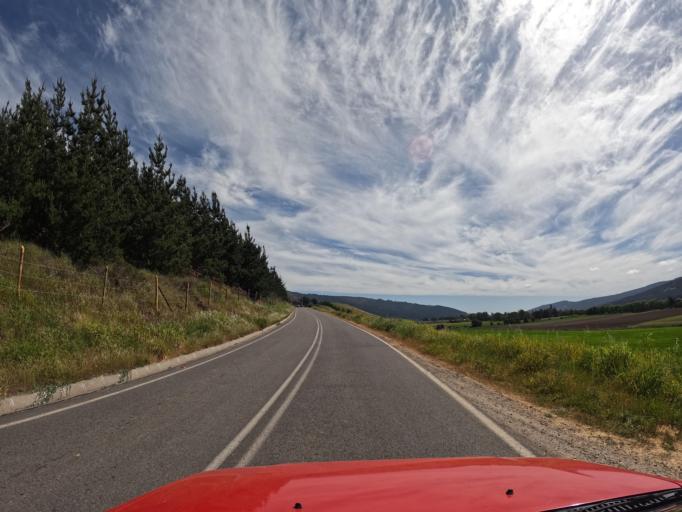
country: CL
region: Maule
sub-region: Provincia de Talca
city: Constitucion
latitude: -35.0395
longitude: -72.0594
